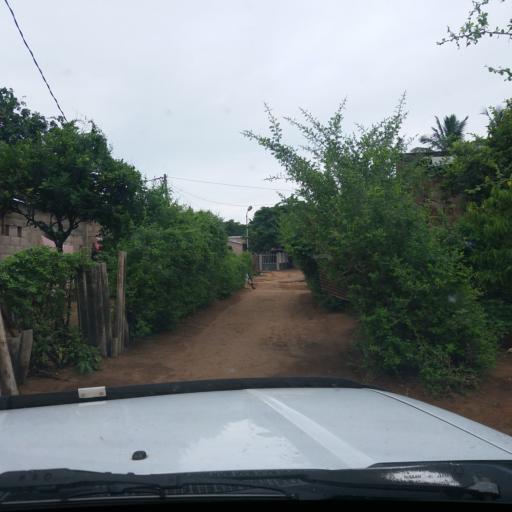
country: MZ
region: Maputo City
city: Maputo
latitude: -25.9106
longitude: 32.5921
